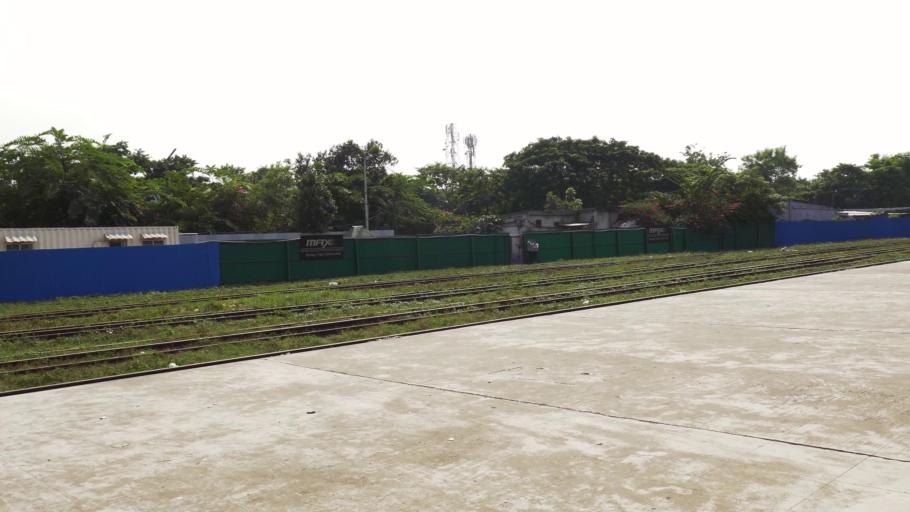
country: BD
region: Dhaka
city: Tungi
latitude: 23.8547
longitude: 90.4065
